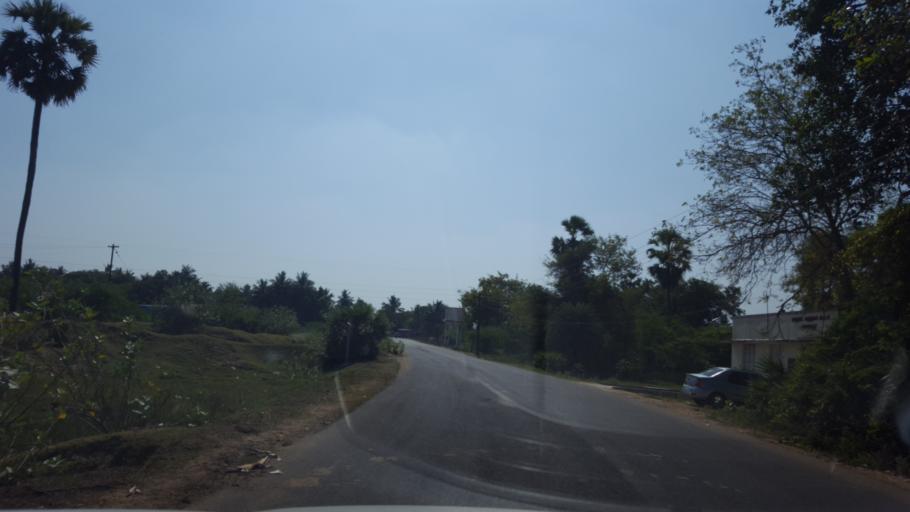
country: IN
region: Tamil Nadu
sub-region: Kancheepuram
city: Kanchipuram
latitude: 12.8386
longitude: 79.7408
